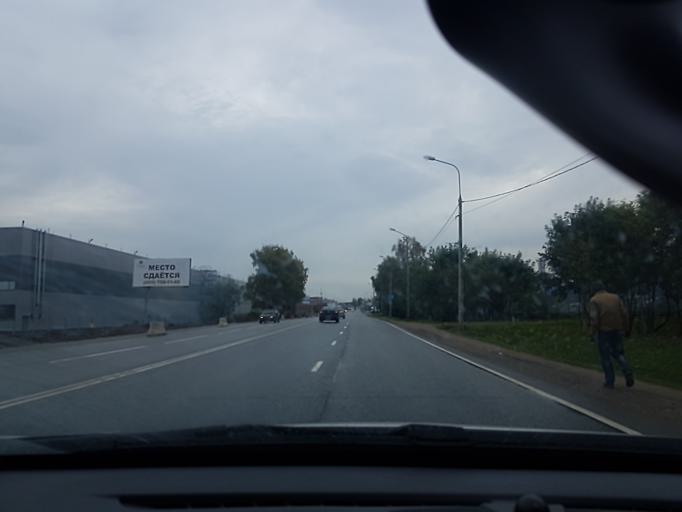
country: RU
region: Moskovskaya
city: Pavlovskaya Sloboda
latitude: 55.8149
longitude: 37.0604
